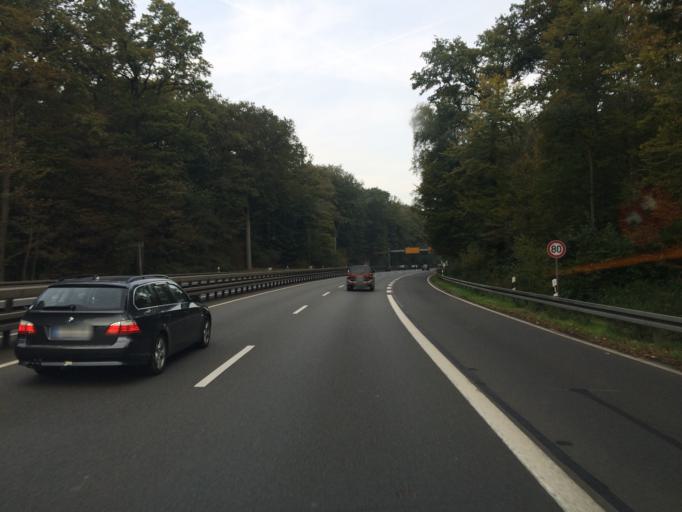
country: DE
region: Lower Saxony
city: Laatzen
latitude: 52.3564
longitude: 9.7863
